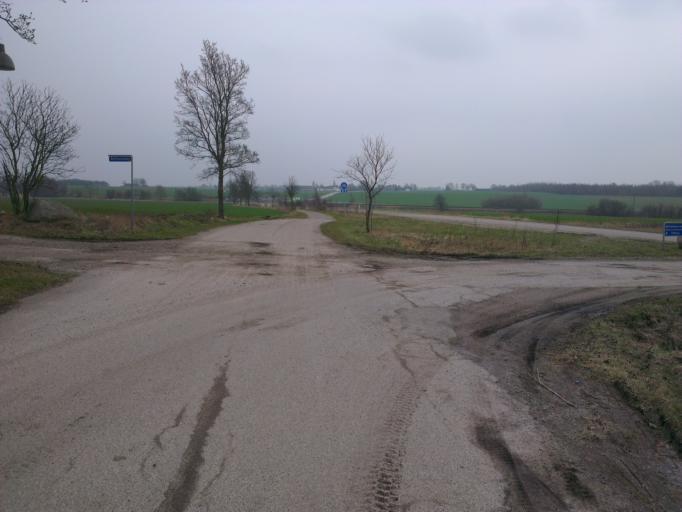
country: DK
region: Capital Region
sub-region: Frederikssund Kommune
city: Frederikssund
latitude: 55.8134
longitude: 12.1056
